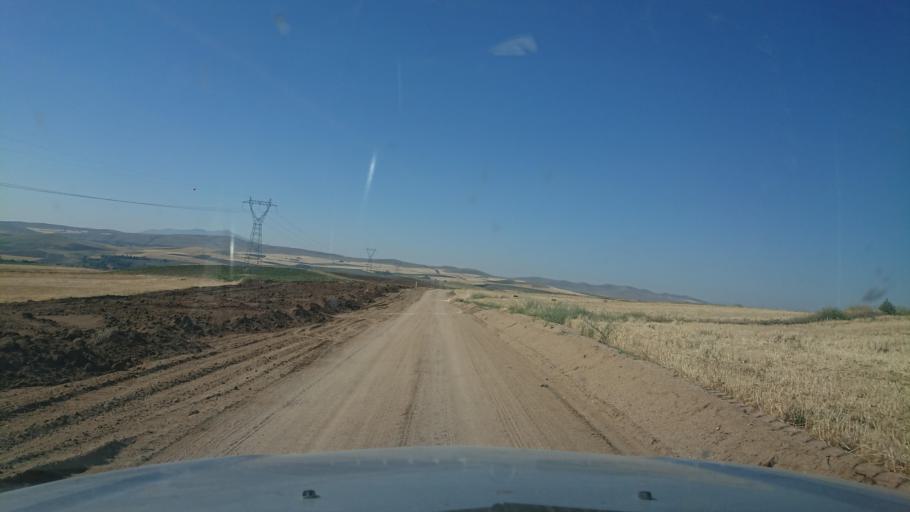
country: TR
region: Aksaray
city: Agacoren
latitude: 38.8391
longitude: 33.9443
